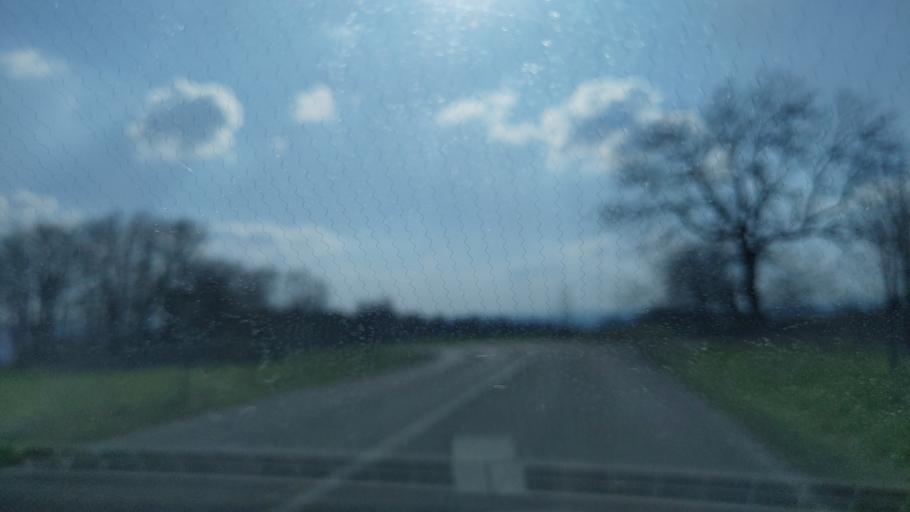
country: CZ
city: Kamenicky Senov
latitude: 50.7677
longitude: 14.4615
